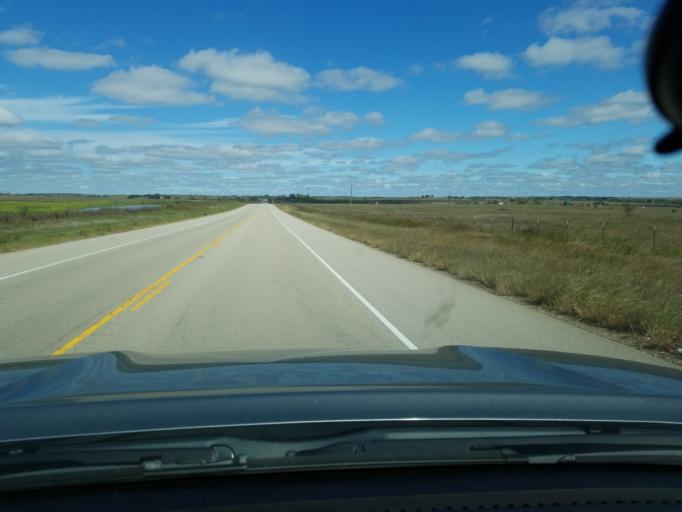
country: US
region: Texas
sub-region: Hamilton County
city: Hamilton
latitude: 31.6326
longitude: -98.1521
